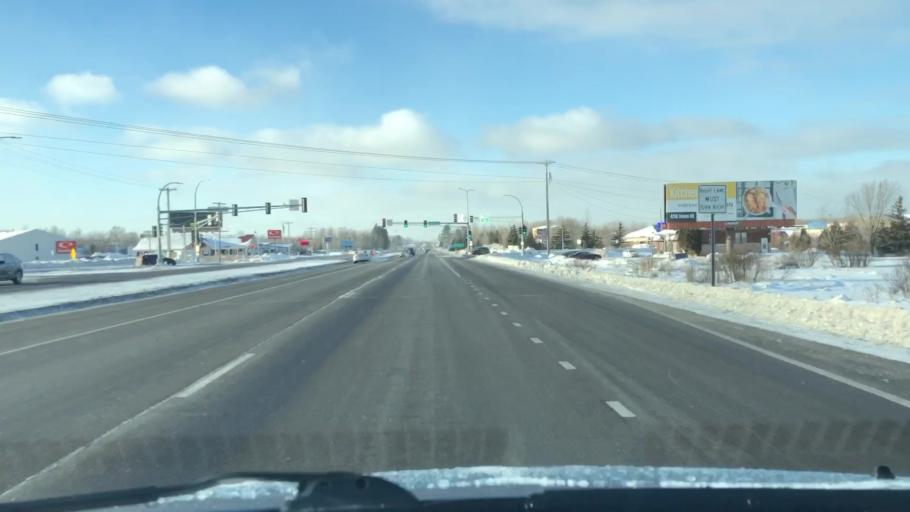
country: US
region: Minnesota
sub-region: Saint Louis County
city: Hermantown
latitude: 46.8142
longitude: -92.1735
